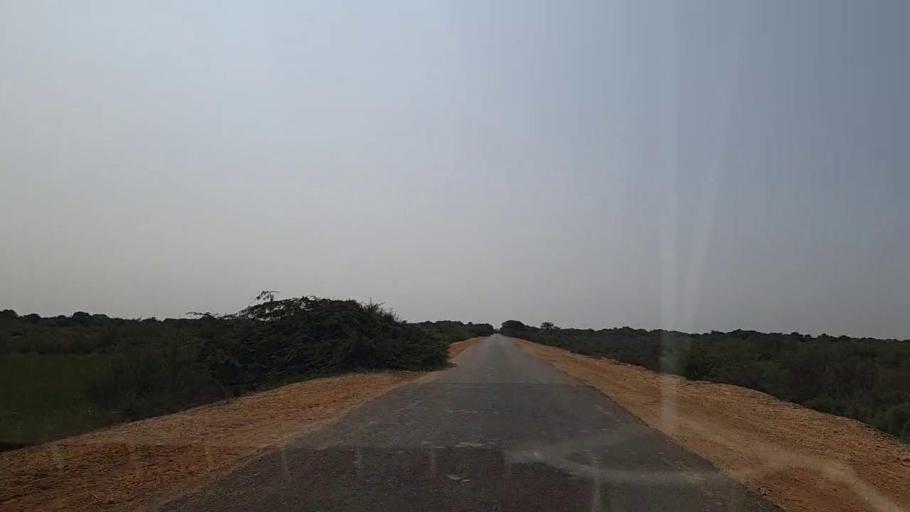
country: PK
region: Sindh
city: Chuhar Jamali
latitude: 24.2715
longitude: 67.9132
